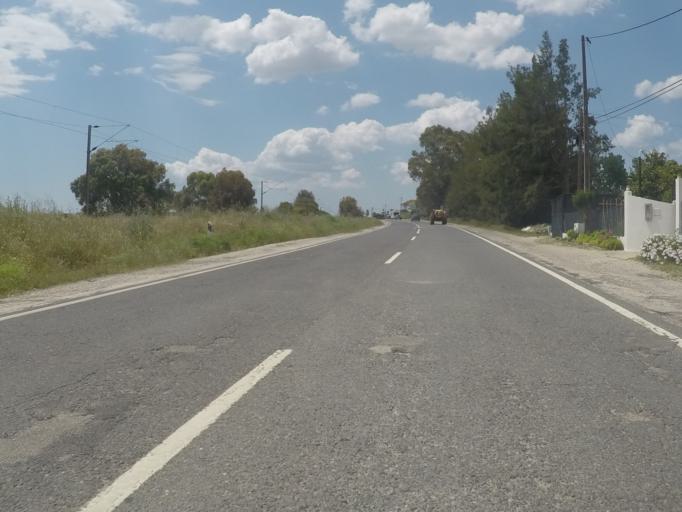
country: PT
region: Setubal
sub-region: Setubal
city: Setubal
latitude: 38.5684
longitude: -8.7672
